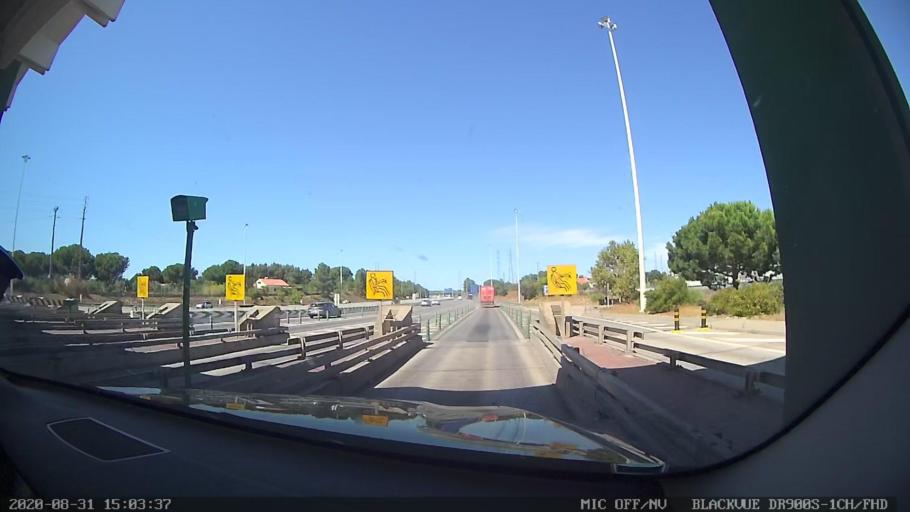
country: PT
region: Setubal
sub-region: Palmela
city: Palmela
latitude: 38.5686
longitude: -8.8662
